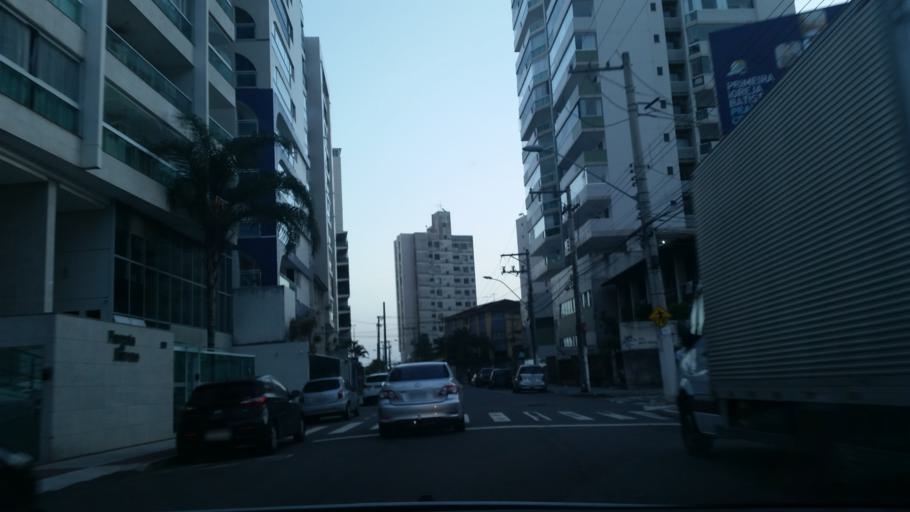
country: BR
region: Espirito Santo
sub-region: Vila Velha
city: Vila Velha
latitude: -20.3299
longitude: -40.2748
